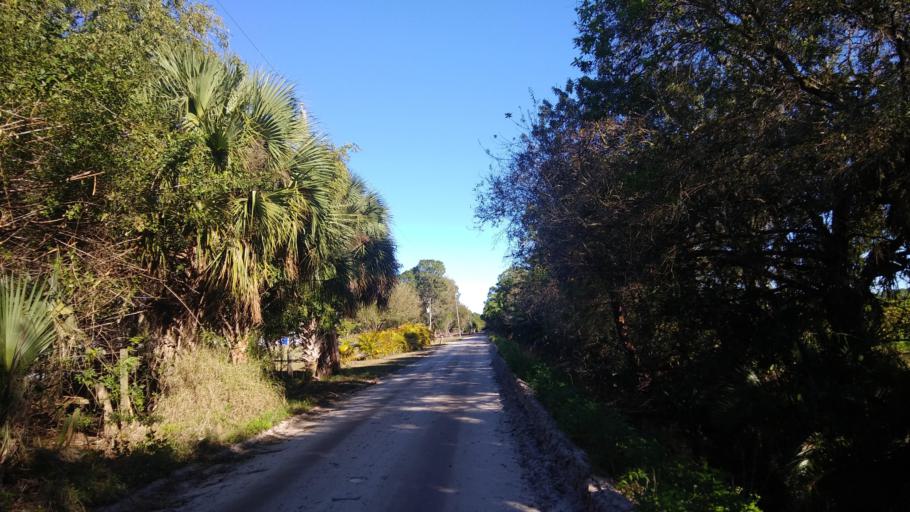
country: US
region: Florida
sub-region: Indian River County
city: Fellsmere
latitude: 27.7536
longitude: -80.5821
